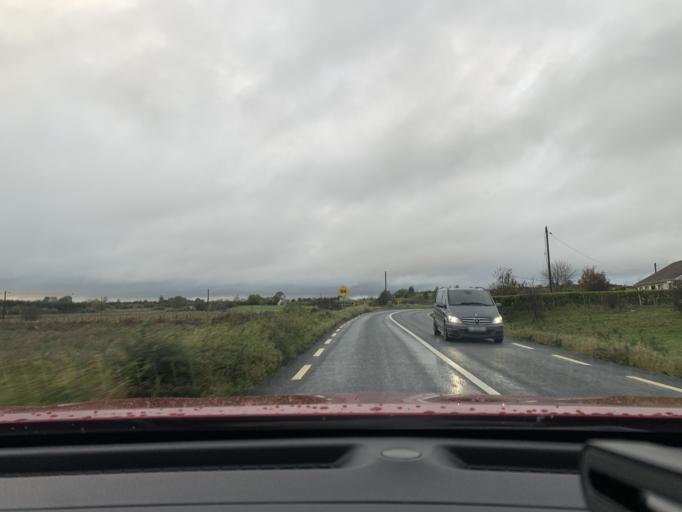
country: IE
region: Connaught
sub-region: Sligo
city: Ballymote
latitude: 54.1153
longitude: -8.5389
